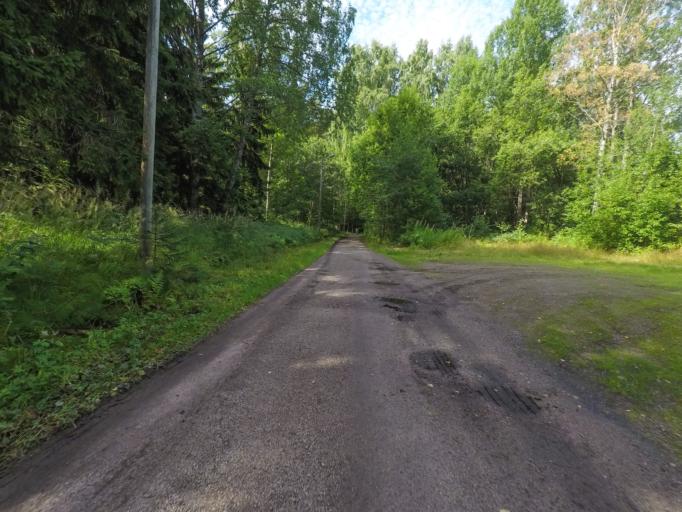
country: FI
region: Uusimaa
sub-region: Helsinki
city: Vantaa
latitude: 60.1676
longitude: 25.0800
